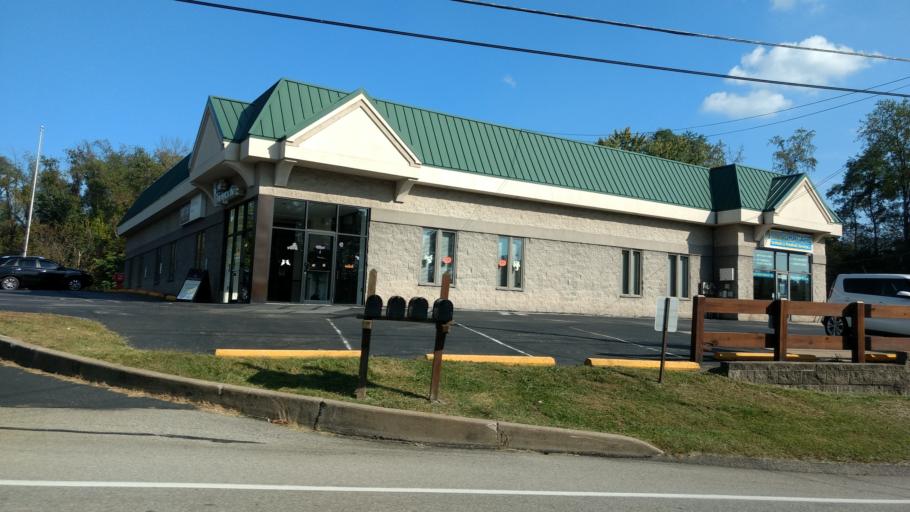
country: US
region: Pennsylvania
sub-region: Westmoreland County
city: Lynnwood-Pricedale
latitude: 40.1339
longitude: -79.8430
